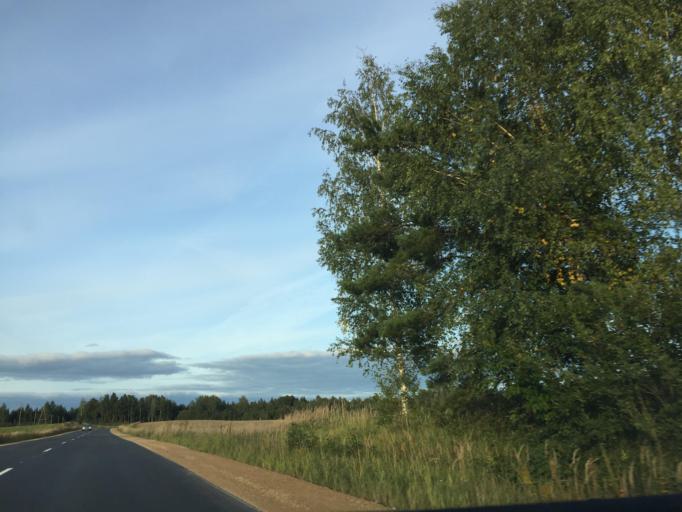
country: LV
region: Viesite
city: Viesite
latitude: 56.3694
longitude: 25.6391
